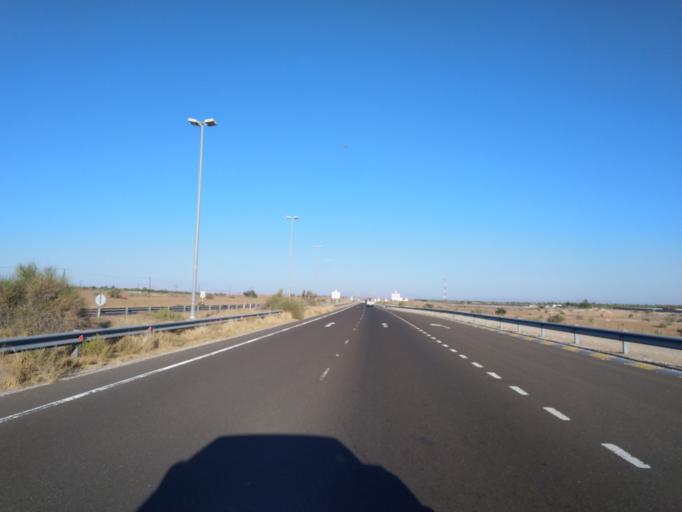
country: OM
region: Al Buraimi
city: Al Buraymi
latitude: 24.5384
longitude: 55.6179
